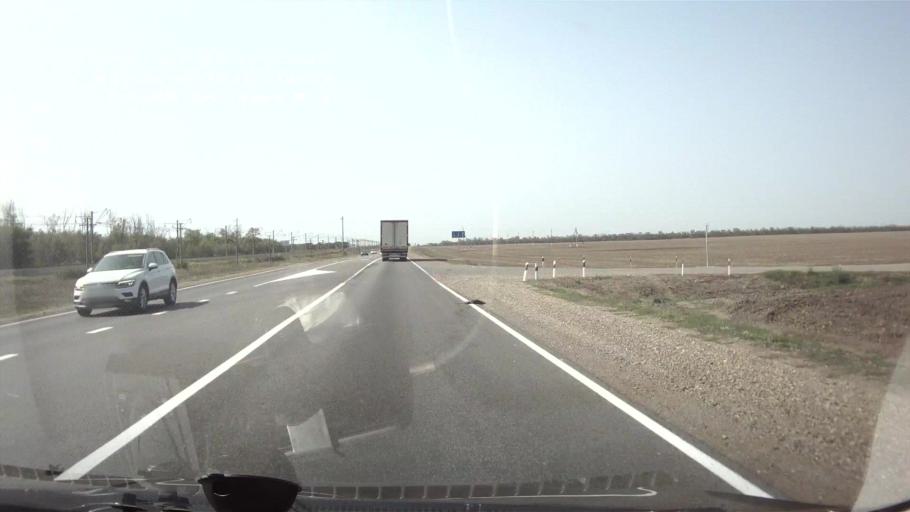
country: RU
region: Krasnodarskiy
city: Ladozhskaya
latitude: 45.3545
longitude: 40.0178
